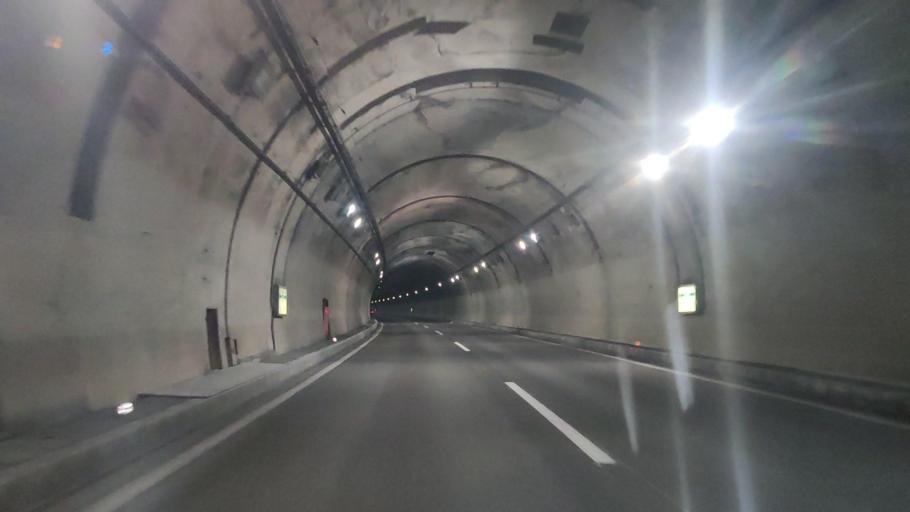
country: JP
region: Oita
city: Beppu
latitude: 33.2694
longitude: 131.3407
